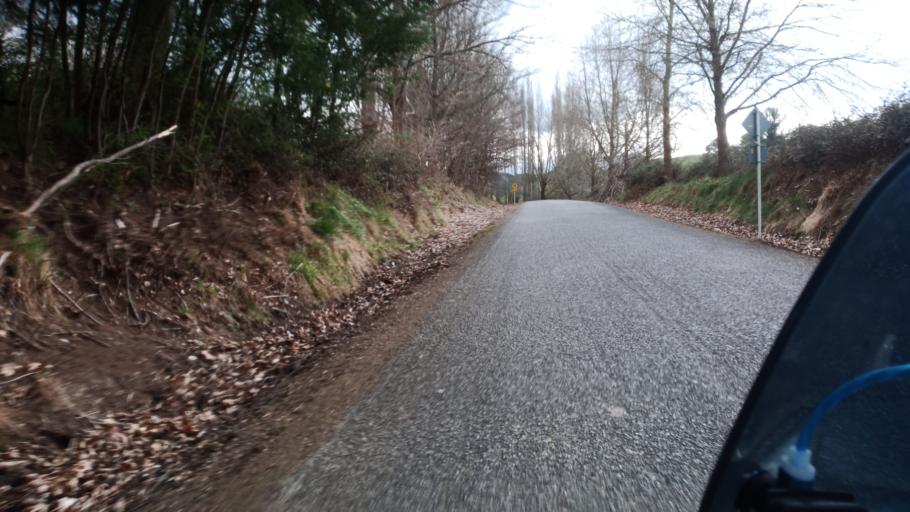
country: NZ
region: Hawke's Bay
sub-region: Wairoa District
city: Wairoa
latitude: -38.7718
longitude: 177.4149
